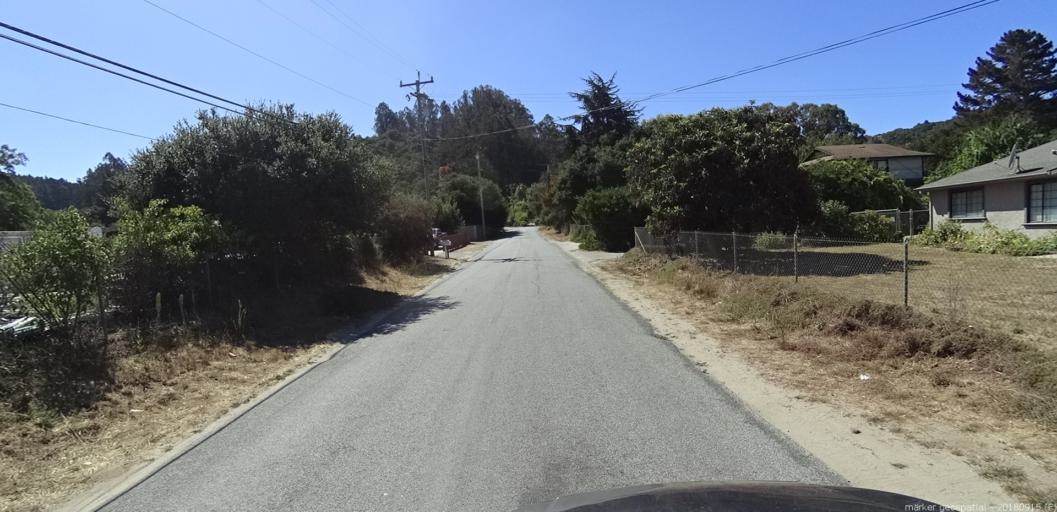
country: US
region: California
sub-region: Monterey County
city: Las Lomas
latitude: 36.8550
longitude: -121.7063
